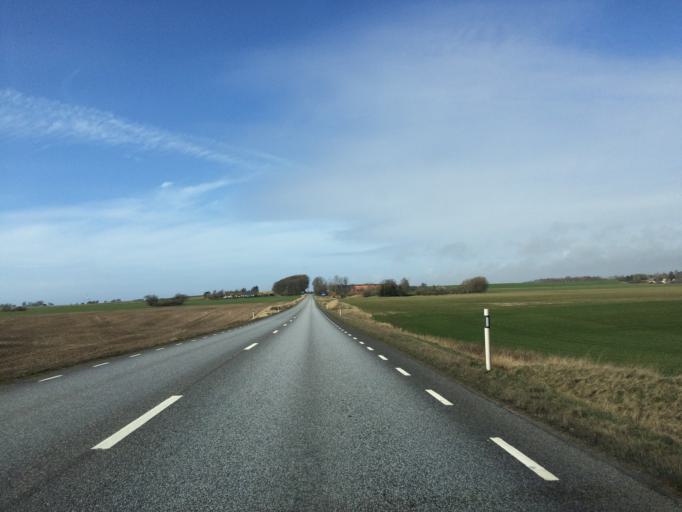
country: SE
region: Halland
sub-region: Halmstads Kommun
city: Paarp
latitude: 56.5834
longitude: 12.9977
